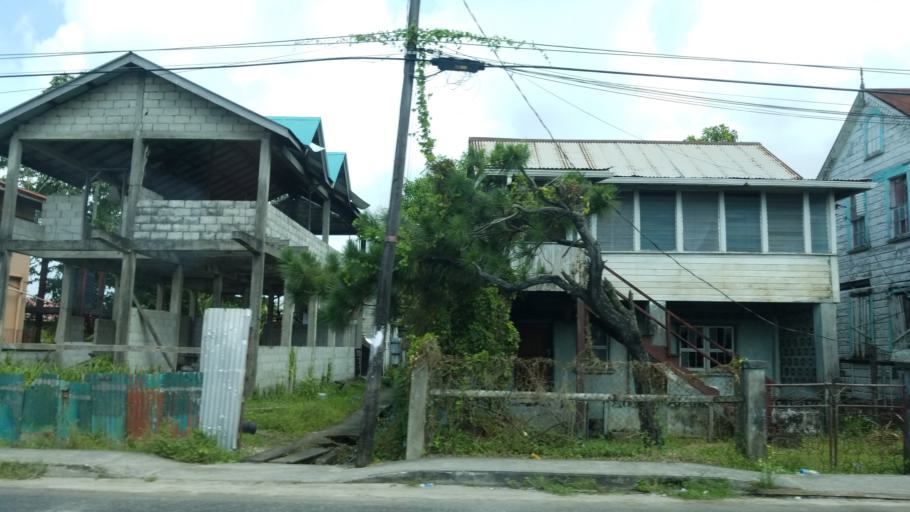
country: GY
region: Demerara-Mahaica
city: Georgetown
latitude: 6.7642
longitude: -58.1778
